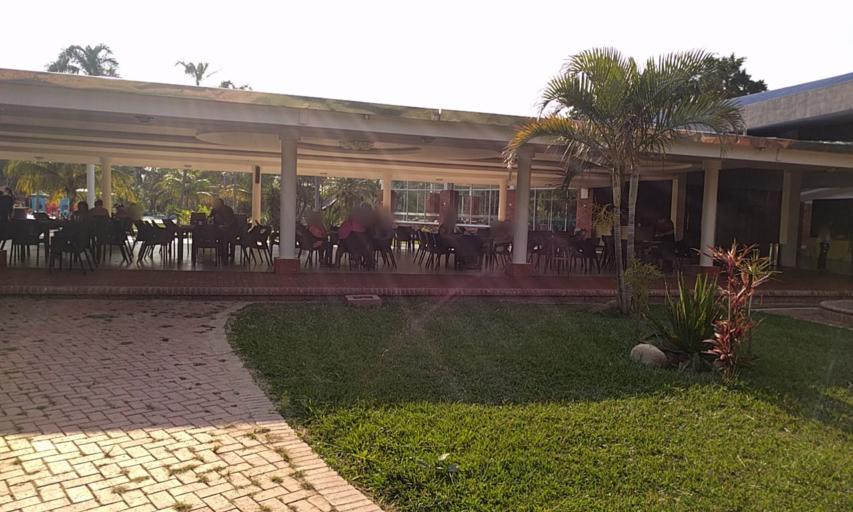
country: BO
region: Santa Cruz
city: Warnes
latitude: -17.4484
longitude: -63.1843
